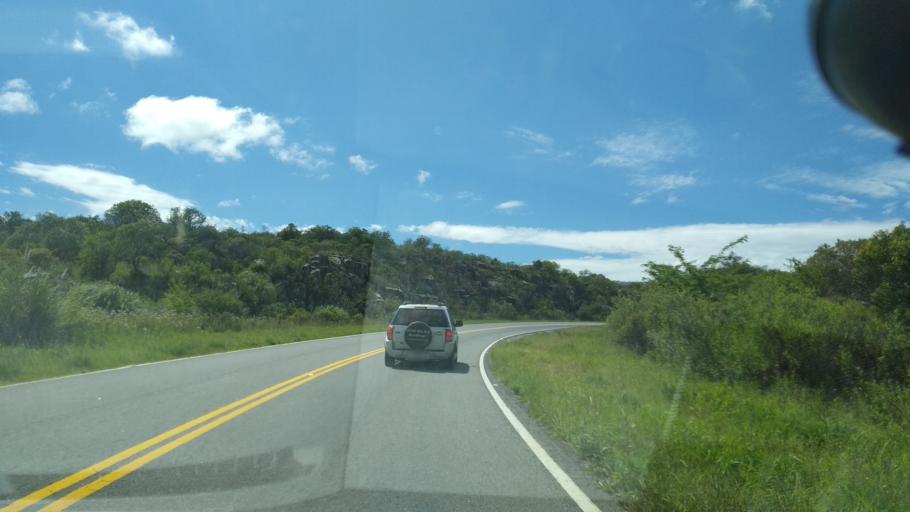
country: AR
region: Cordoba
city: Mina Clavero
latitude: -31.7552
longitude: -64.9574
